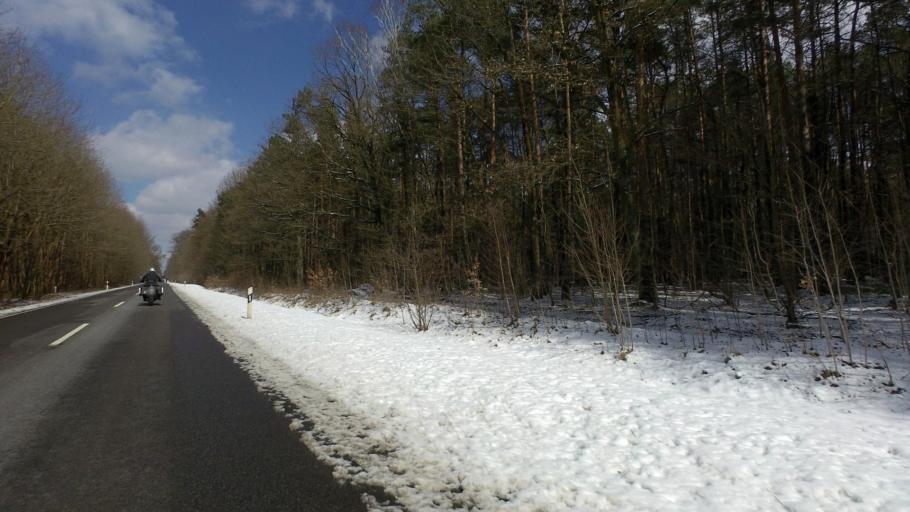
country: DE
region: Brandenburg
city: Eberswalde
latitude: 52.7897
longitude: 13.8383
